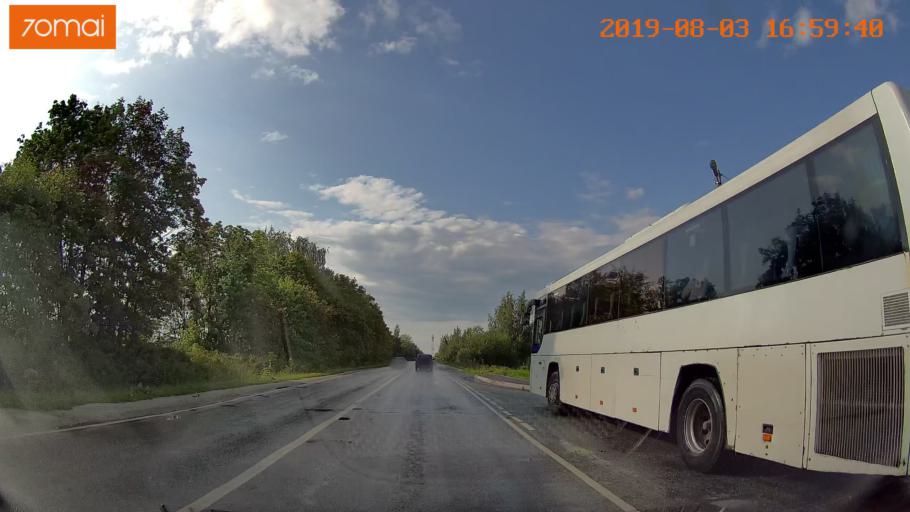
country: RU
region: Moskovskaya
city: Voskresensk
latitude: 55.3315
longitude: 38.6226
